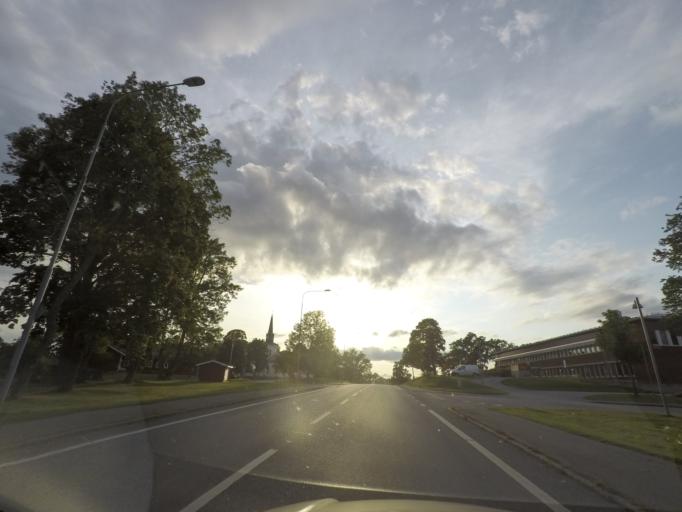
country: SE
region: OErebro
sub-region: Lindesbergs Kommun
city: Frovi
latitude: 59.4615
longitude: 15.3751
